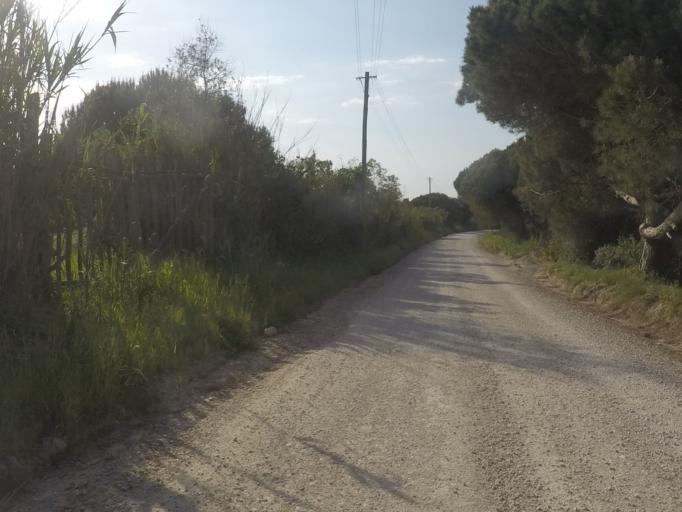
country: PT
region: Setubal
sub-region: Sesimbra
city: Sesimbra
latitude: 38.4384
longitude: -9.1902
